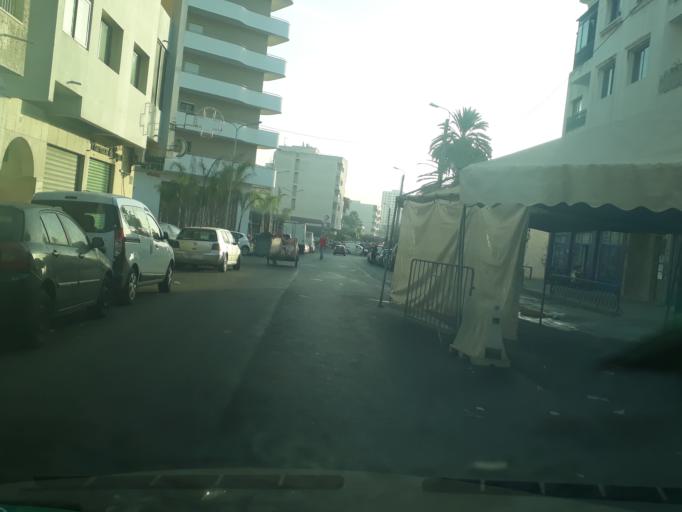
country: MA
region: Grand Casablanca
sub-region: Casablanca
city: Casablanca
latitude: 33.5803
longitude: -7.6334
